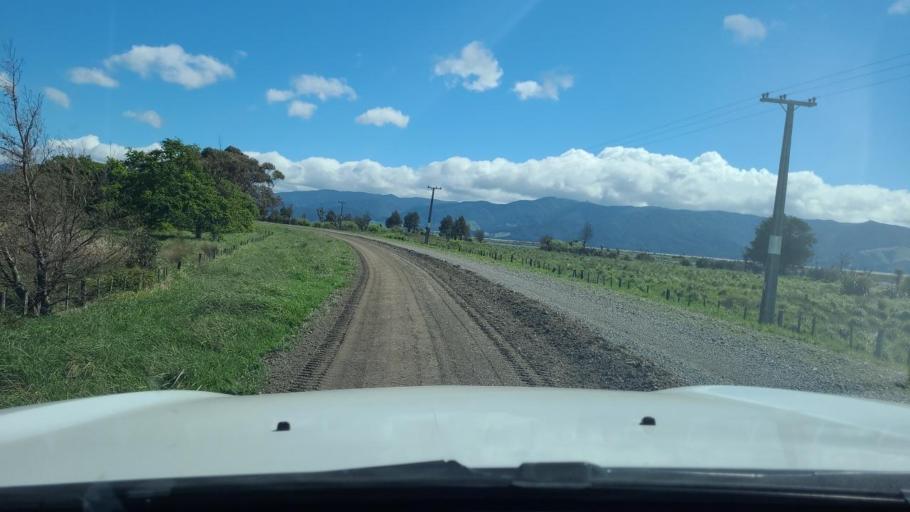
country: NZ
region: Wellington
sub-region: Upper Hutt City
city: Upper Hutt
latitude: -41.2419
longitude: 175.2684
